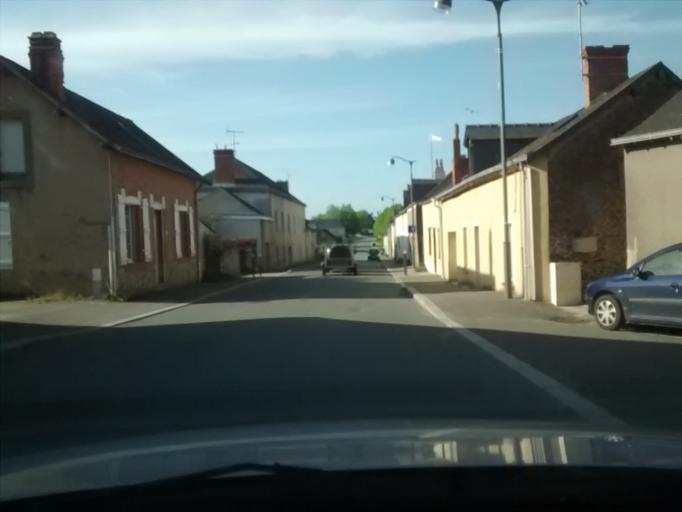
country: FR
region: Pays de la Loire
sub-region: Departement de la Mayenne
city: Soulge-sur-Ouette
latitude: 48.0177
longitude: -0.5814
